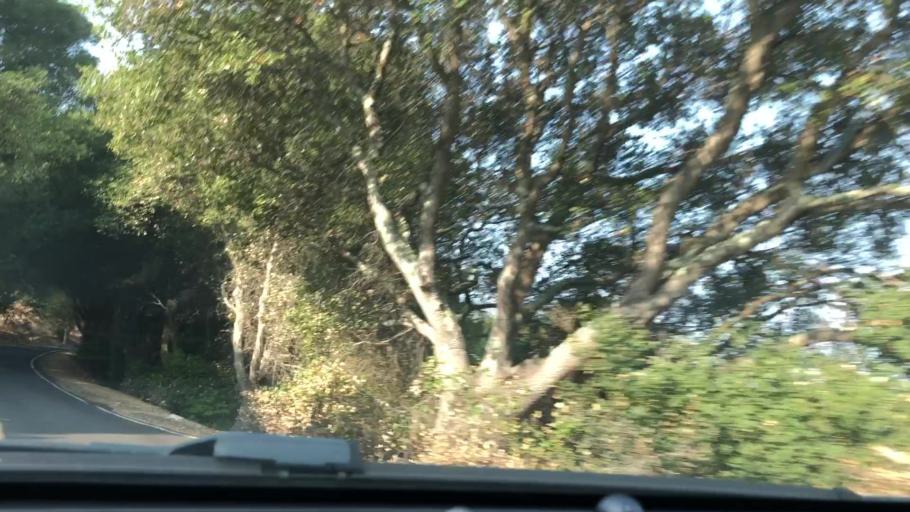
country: US
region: California
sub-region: Alameda County
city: Berkeley
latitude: 37.8990
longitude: -122.2317
